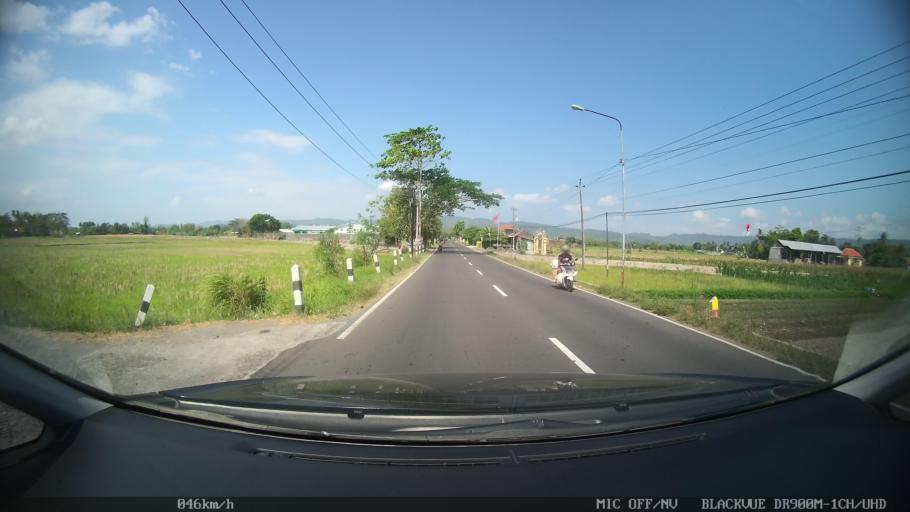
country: ID
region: Daerah Istimewa Yogyakarta
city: Bantul
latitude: -7.9100
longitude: 110.3542
